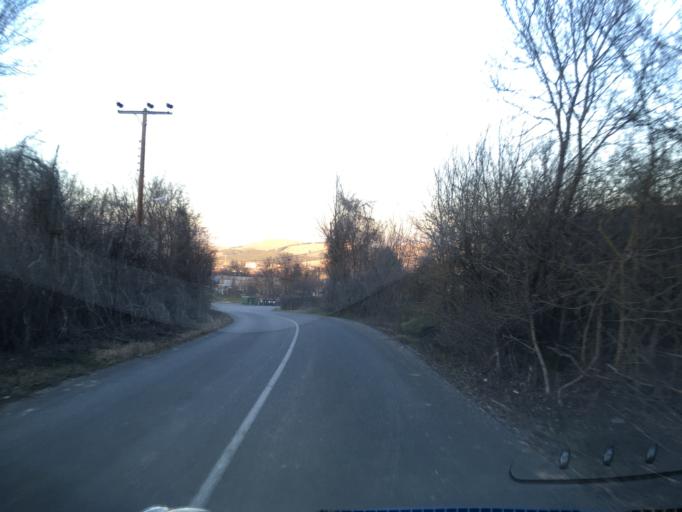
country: GR
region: West Macedonia
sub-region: Nomos Kozanis
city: Koila
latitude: 40.3274
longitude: 21.8021
